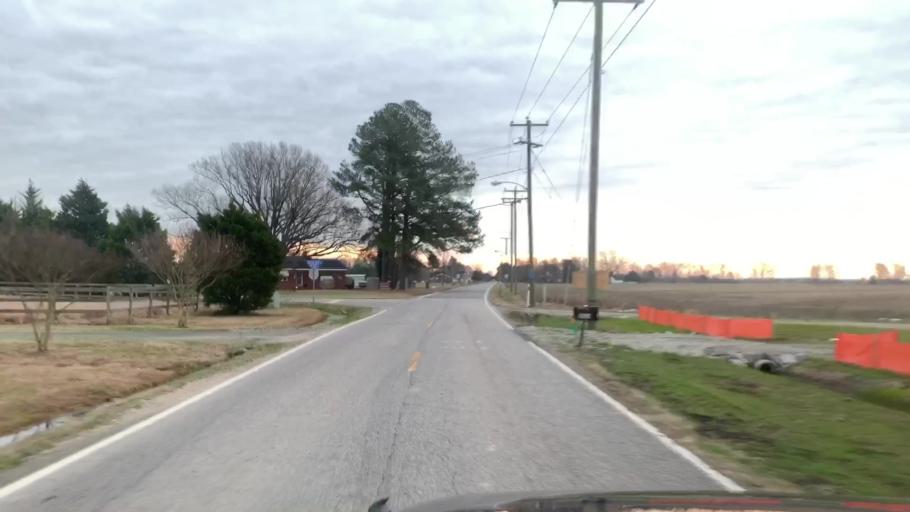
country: US
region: North Carolina
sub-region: Currituck County
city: Moyock
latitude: 36.6283
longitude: -76.1695
